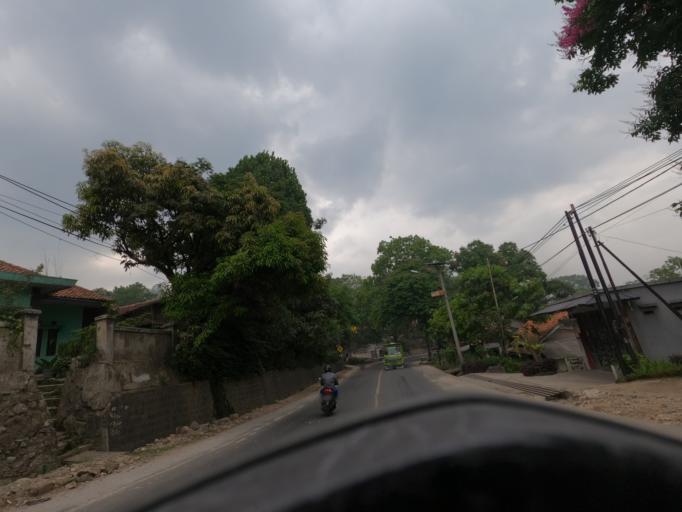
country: ID
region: West Java
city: Padalarang
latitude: -6.8322
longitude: 107.4387
